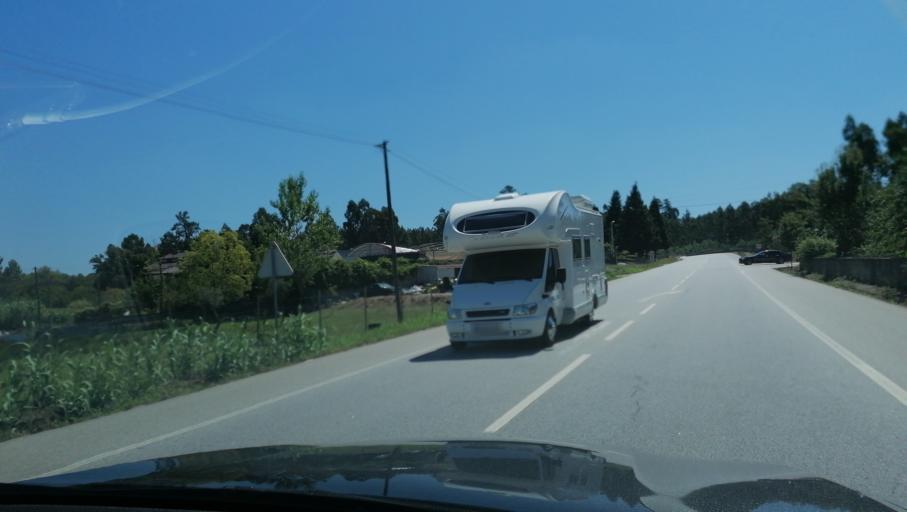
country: PT
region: Aveiro
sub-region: Agueda
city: Aguada de Cima
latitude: 40.5064
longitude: -8.4462
